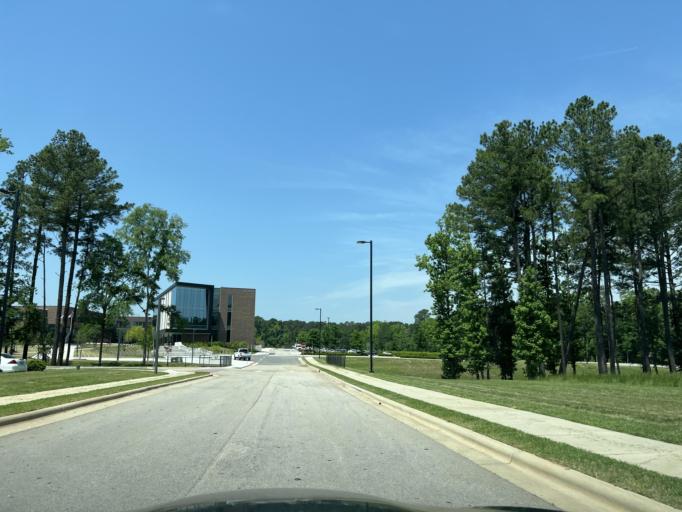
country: US
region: North Carolina
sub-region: Wake County
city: Morrisville
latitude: 35.8535
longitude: -78.8377
